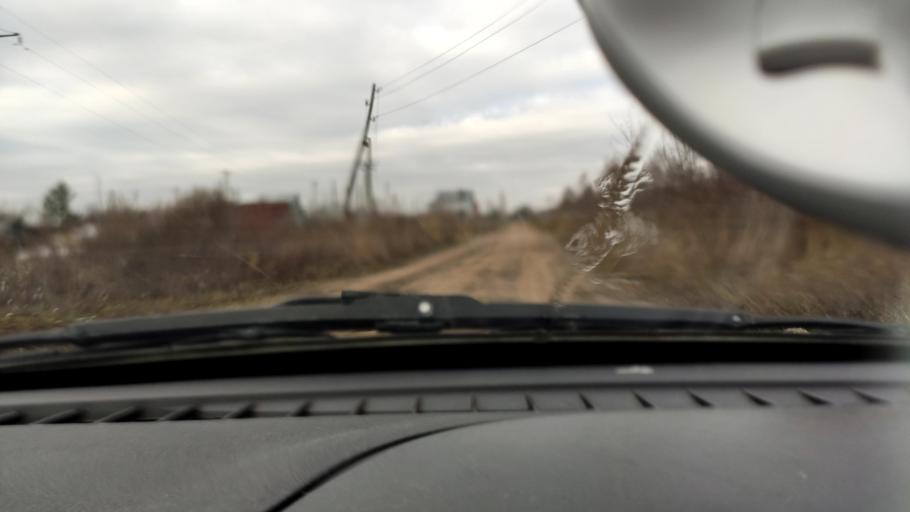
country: RU
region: Perm
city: Kondratovo
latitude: 57.9886
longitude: 56.0781
